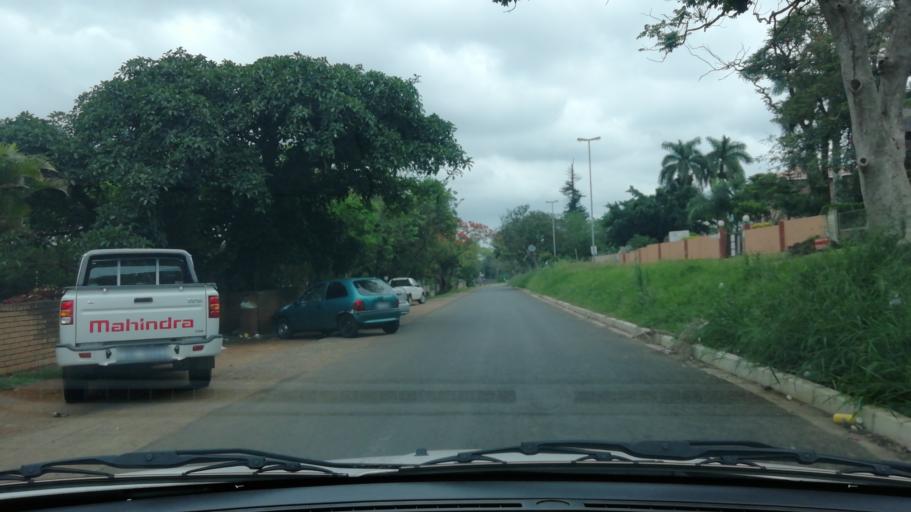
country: ZA
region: KwaZulu-Natal
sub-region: uThungulu District Municipality
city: Empangeni
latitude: -28.7527
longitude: 31.8955
